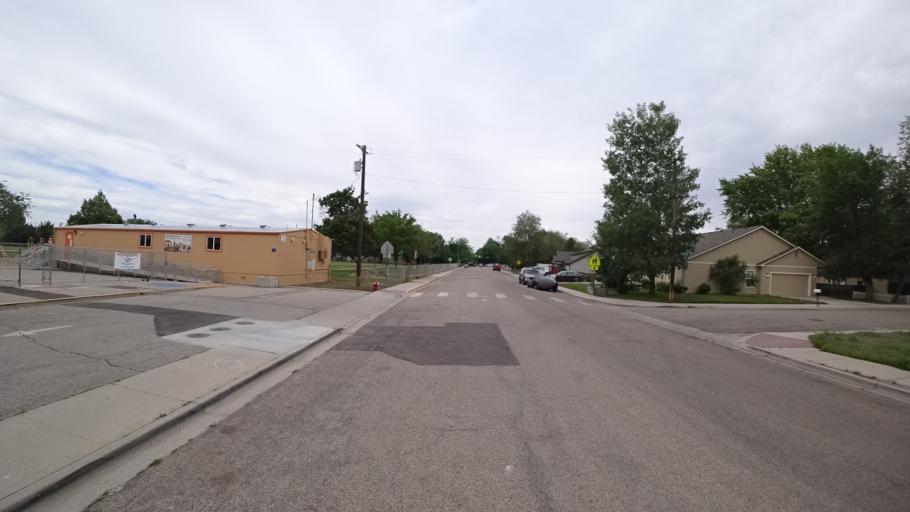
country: US
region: Idaho
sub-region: Ada County
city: Boise
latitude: 43.5825
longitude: -116.2112
